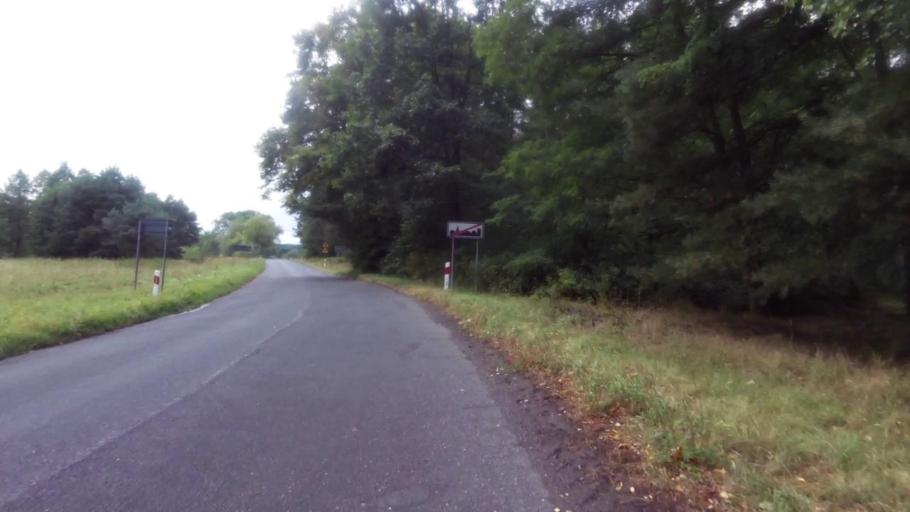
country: PL
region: West Pomeranian Voivodeship
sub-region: Powiat mysliborski
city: Boleszkowice
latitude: 52.6862
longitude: 14.6259
